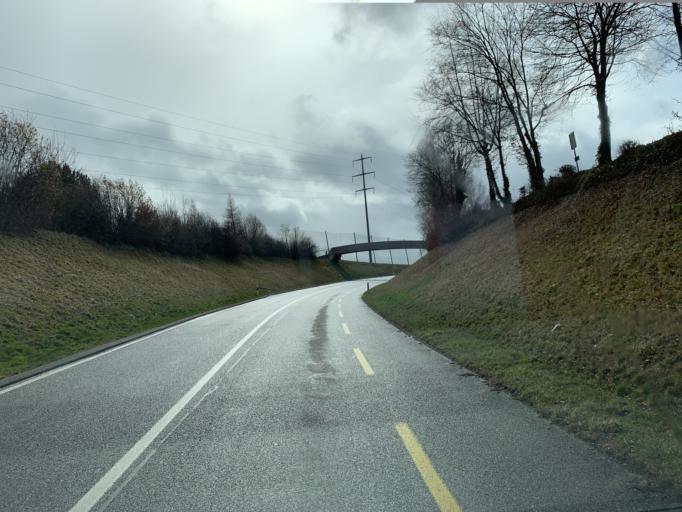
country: CH
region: Fribourg
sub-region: Sense District
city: Dudingen
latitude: 46.8806
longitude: 7.1926
